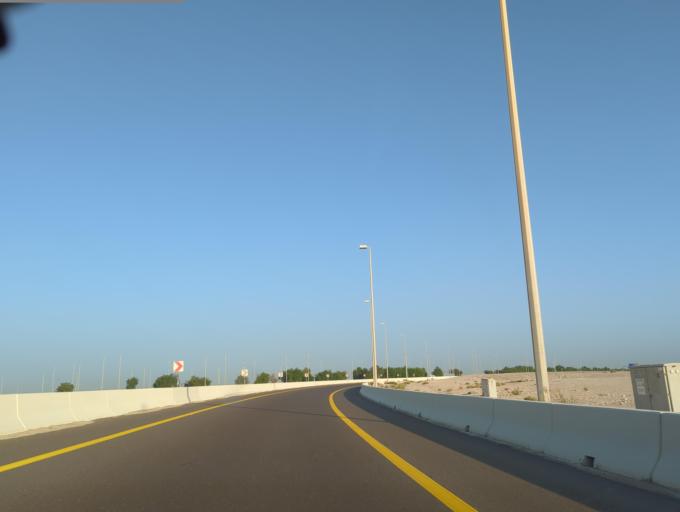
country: AE
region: Abu Dhabi
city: Abu Dhabi
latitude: 24.4124
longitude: 54.6772
